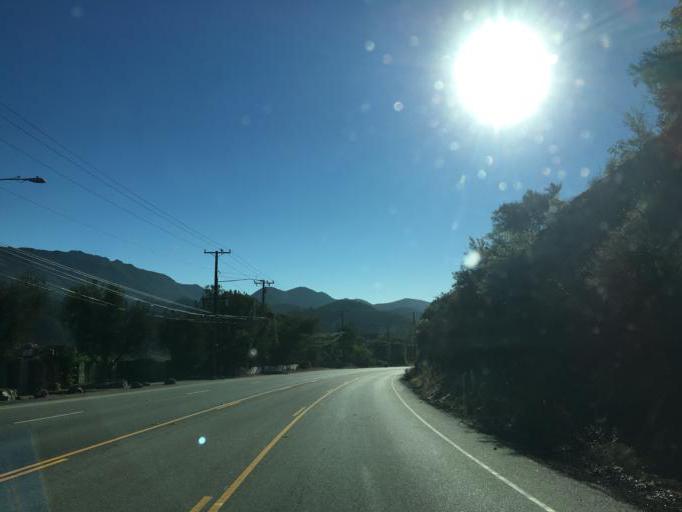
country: US
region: California
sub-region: Los Angeles County
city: Agoura Hills
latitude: 34.1195
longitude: -118.7942
